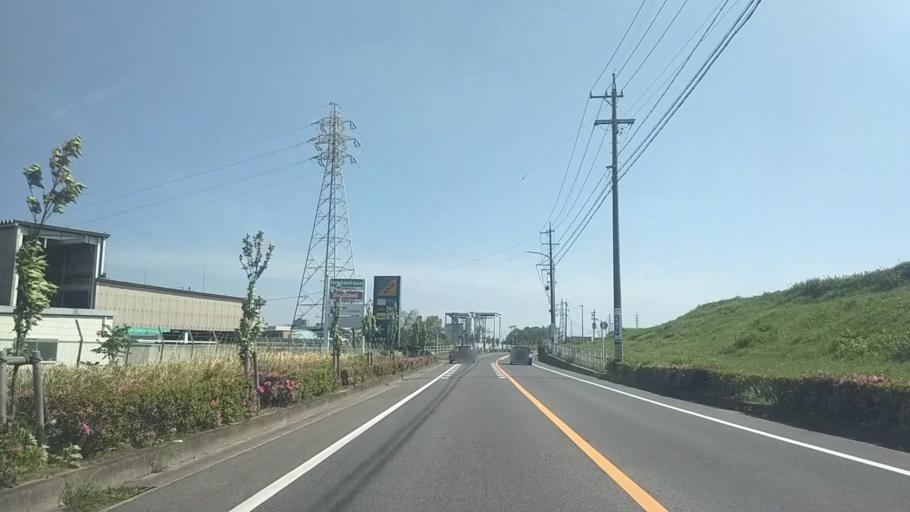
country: JP
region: Aichi
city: Okazaki
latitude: 34.9800
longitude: 137.1502
